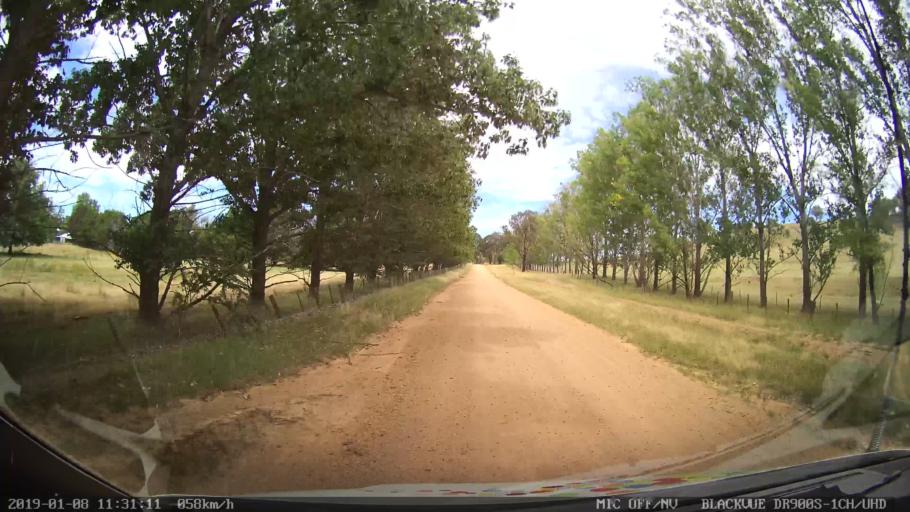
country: AU
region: New South Wales
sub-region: Guyra
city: Guyra
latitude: -30.3113
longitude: 151.5392
